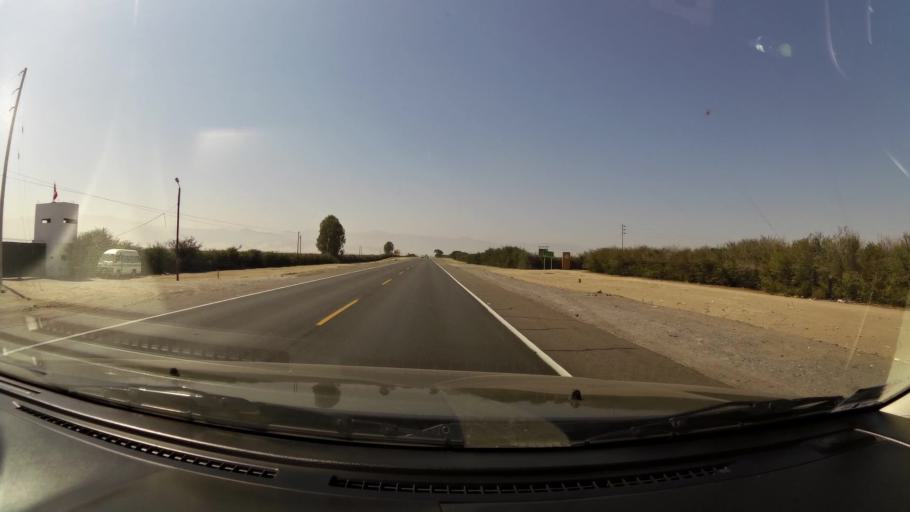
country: PE
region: Ica
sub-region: Provincia de Ica
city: Guadalupe
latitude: -13.9374
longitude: -75.8279
